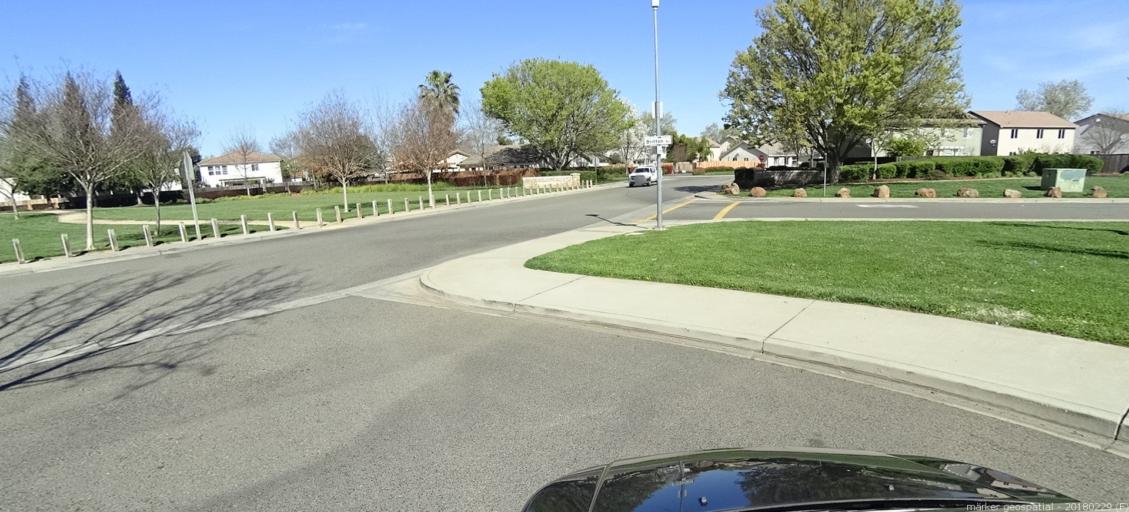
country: US
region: California
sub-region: Sacramento County
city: Rancho Cordova
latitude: 38.5457
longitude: -121.2782
